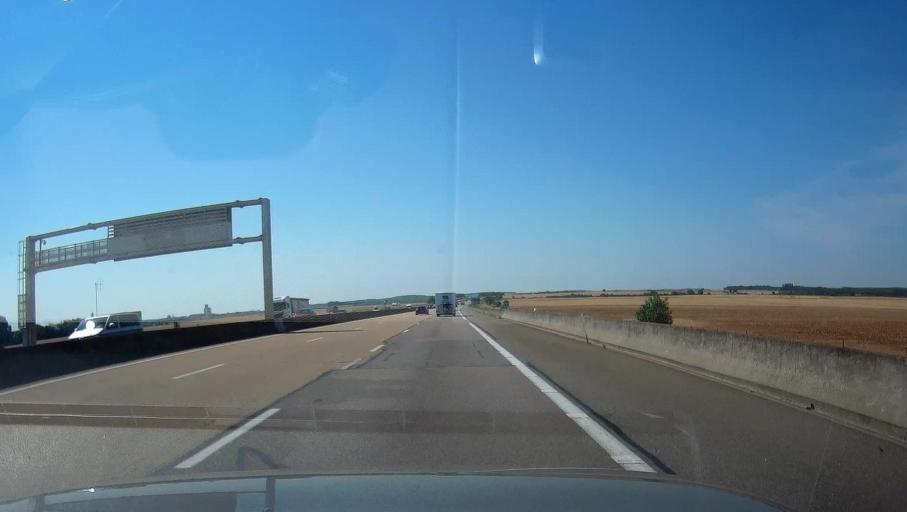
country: FR
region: Bourgogne
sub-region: Departement de la Cote-d'Or
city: Marcilly-sur-Tille
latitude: 47.5128
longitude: 5.1959
